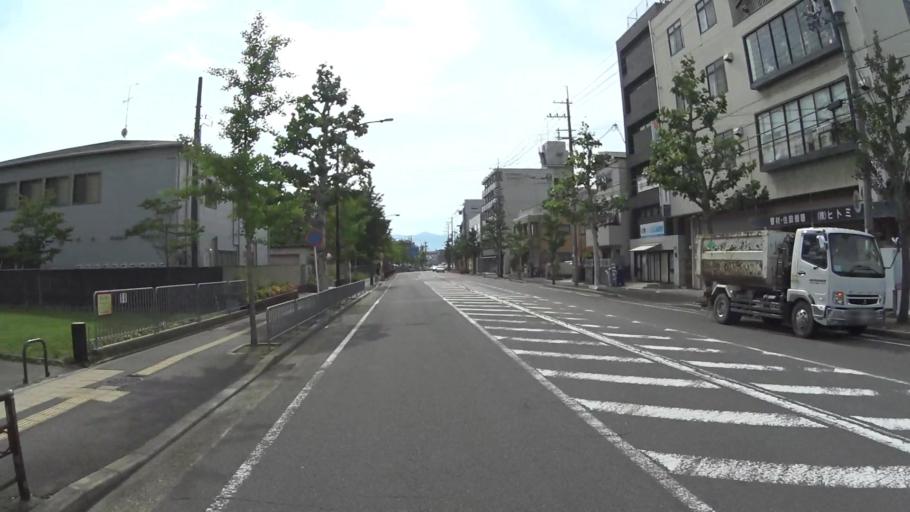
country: JP
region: Kyoto
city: Muko
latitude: 34.9573
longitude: 135.7635
